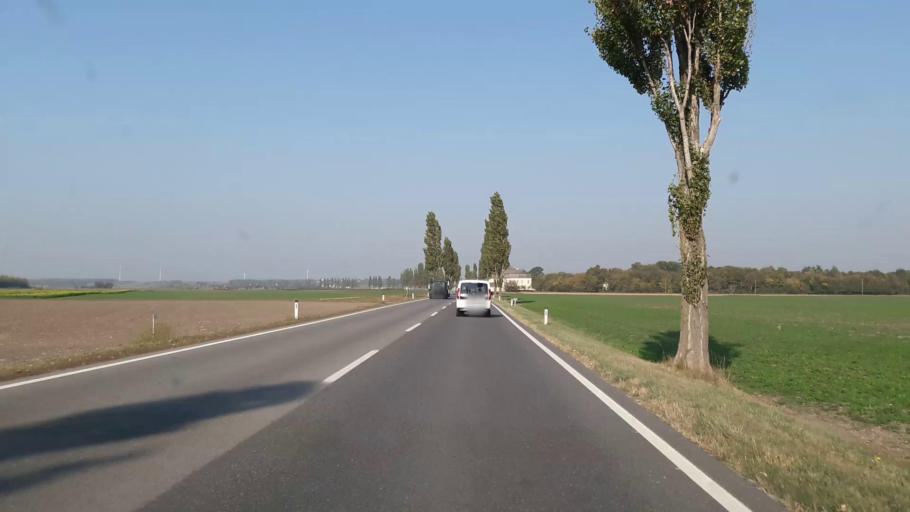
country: AT
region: Lower Austria
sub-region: Politischer Bezirk Ganserndorf
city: Engelhartstetten
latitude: 48.1923
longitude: 16.8979
